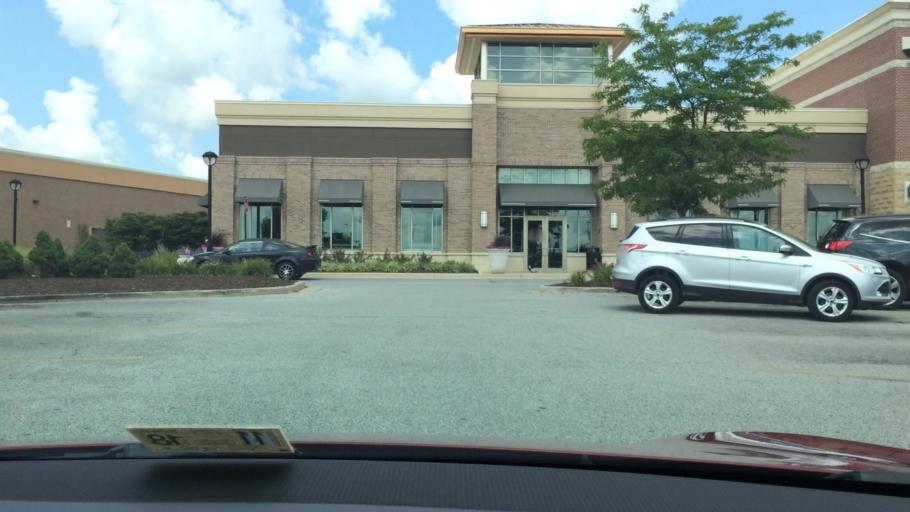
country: US
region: Indiana
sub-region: Saint Joseph County
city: Georgetown
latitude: 41.7178
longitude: -86.1894
